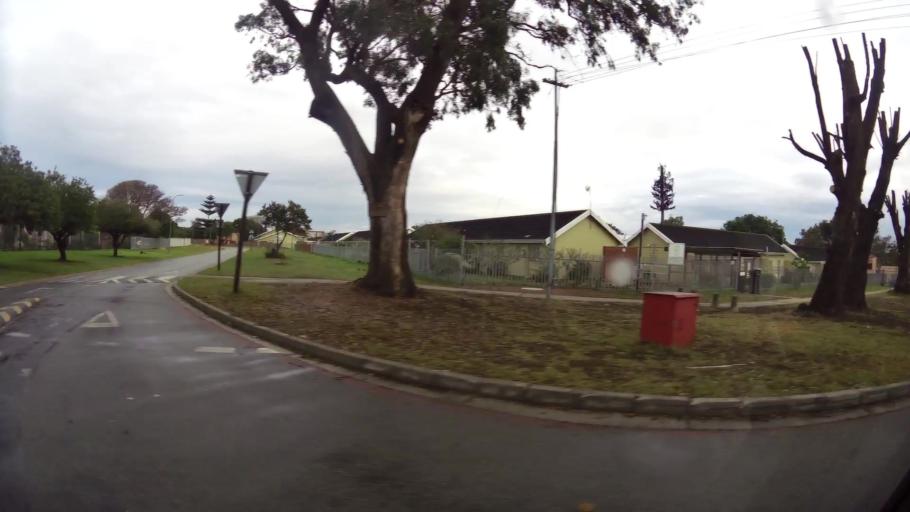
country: ZA
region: Eastern Cape
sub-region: Nelson Mandela Bay Metropolitan Municipality
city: Port Elizabeth
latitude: -33.9832
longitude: 25.5635
